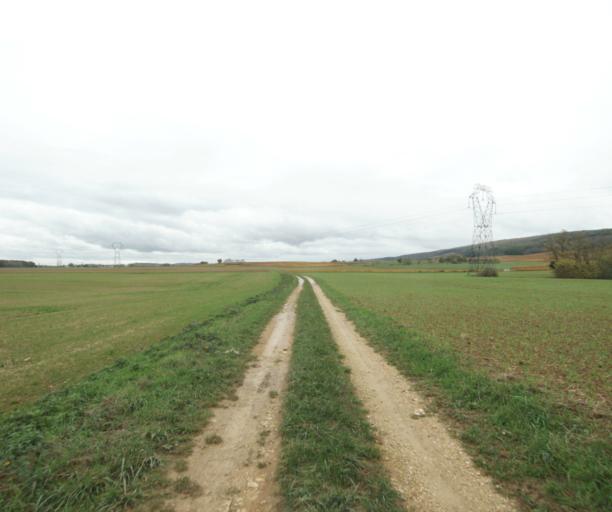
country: FR
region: Bourgogne
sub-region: Departement de Saone-et-Loire
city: Saint-Martin-Belle-Roche
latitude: 46.4667
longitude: 4.8599
